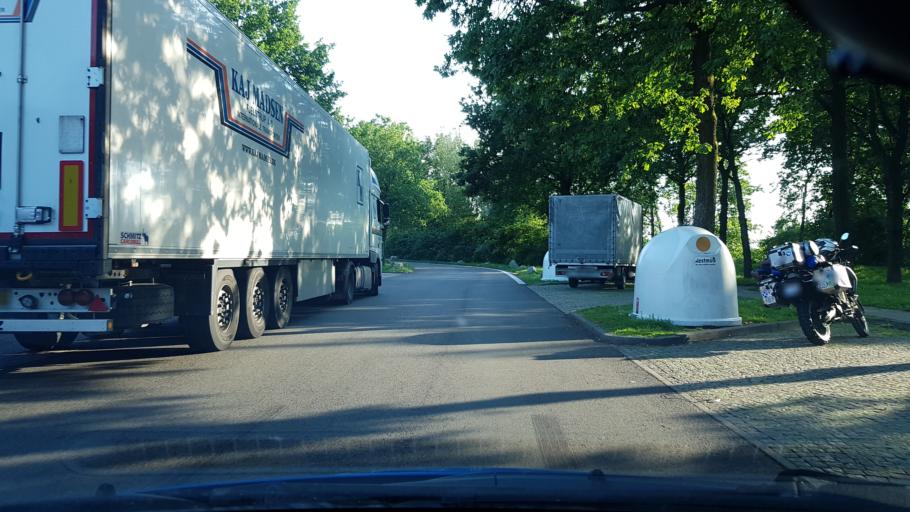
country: DE
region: Lower Saxony
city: Buchholz in der Nordheide
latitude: 53.3905
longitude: 9.8811
